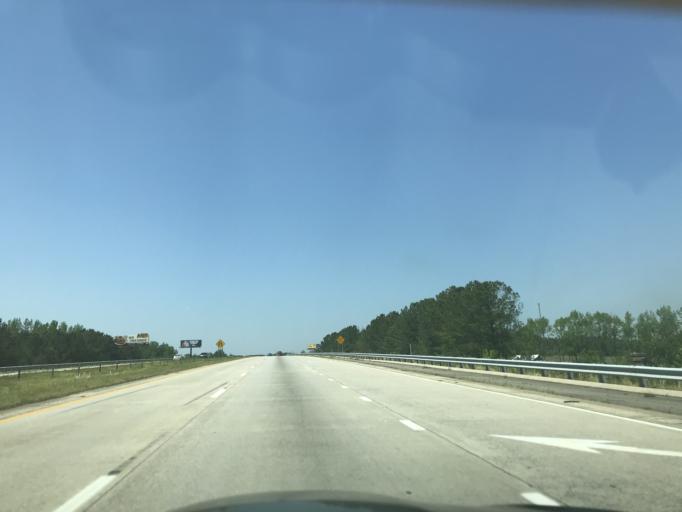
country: US
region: North Carolina
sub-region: Johnston County
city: Benson
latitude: 35.4025
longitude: -78.5232
